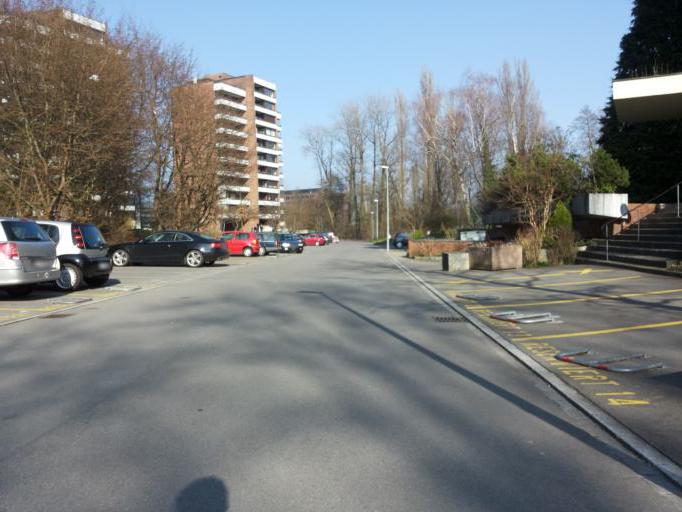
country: CH
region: Zug
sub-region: Zug
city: Cham
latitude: 47.1839
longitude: 8.4746
